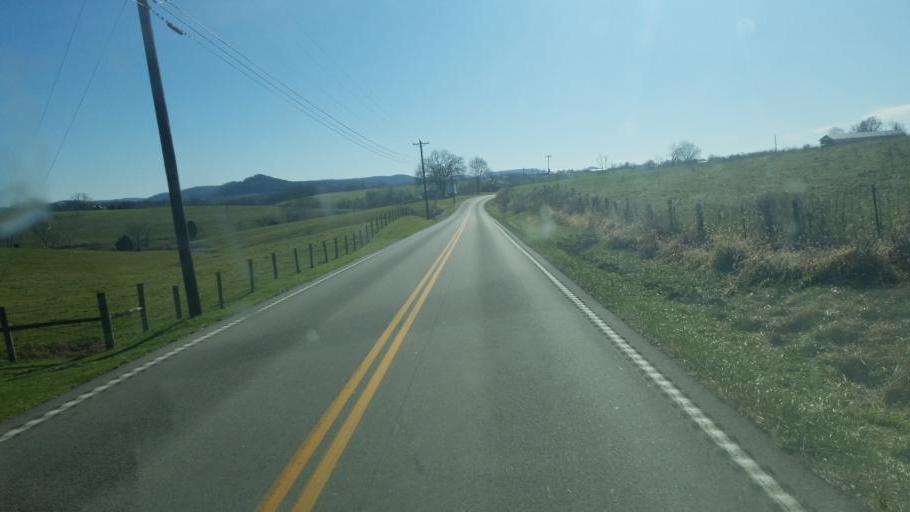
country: US
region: Kentucky
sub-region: Fleming County
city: Flemingsburg
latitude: 38.5105
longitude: -83.6212
